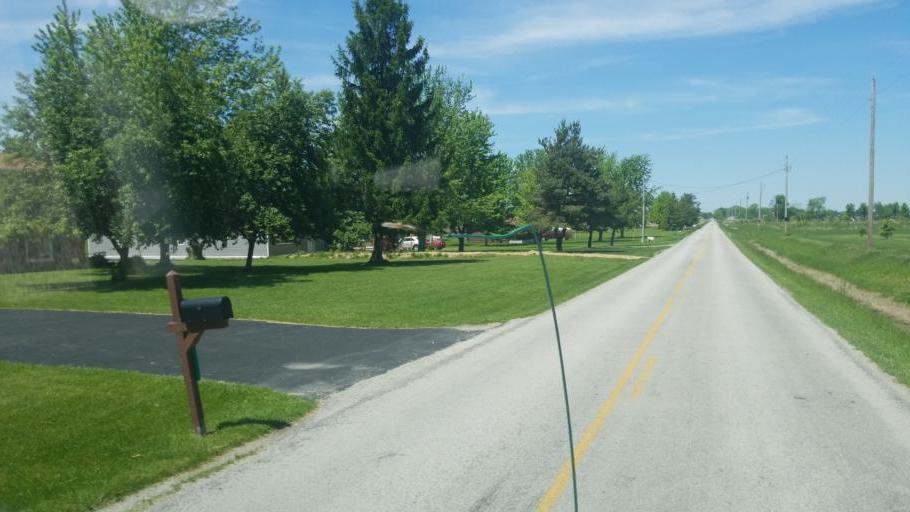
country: US
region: Ohio
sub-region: Huron County
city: Greenwich
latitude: 41.1397
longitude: -82.5383
